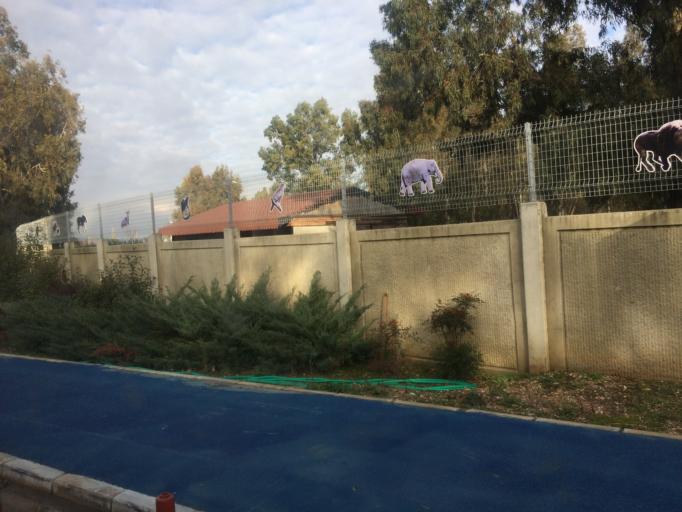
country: TR
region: Izmir
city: Karsiyaka
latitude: 38.4904
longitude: 26.9578
